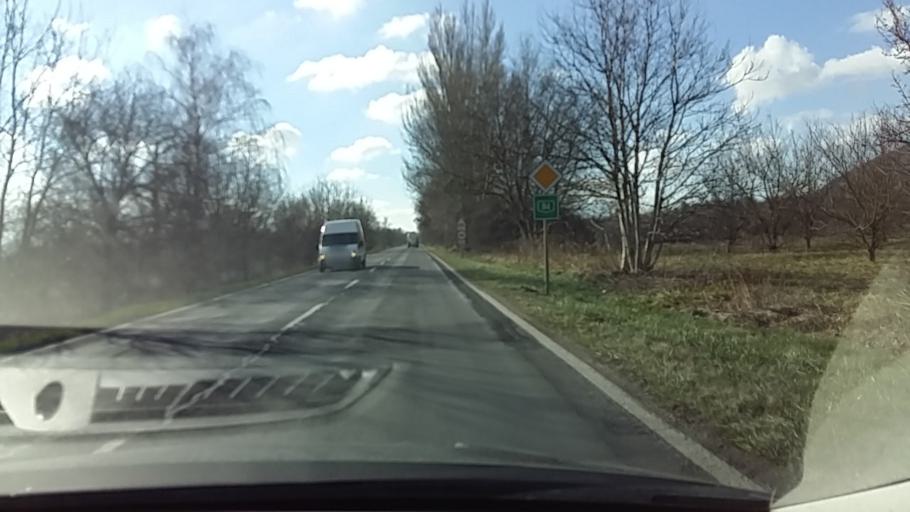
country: HU
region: Veszprem
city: Tapolca
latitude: 46.8196
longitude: 17.3814
